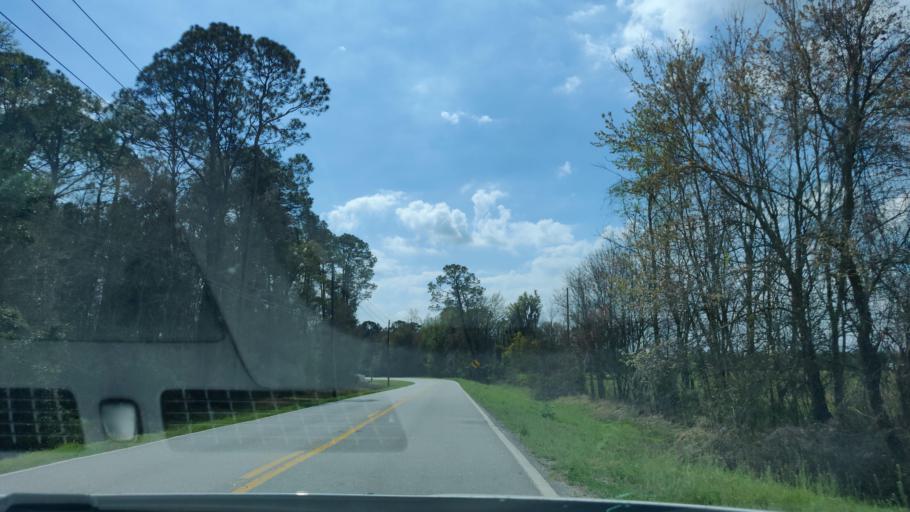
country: US
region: Florida
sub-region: Duval County
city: Baldwin
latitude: 30.2501
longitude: -81.9492
